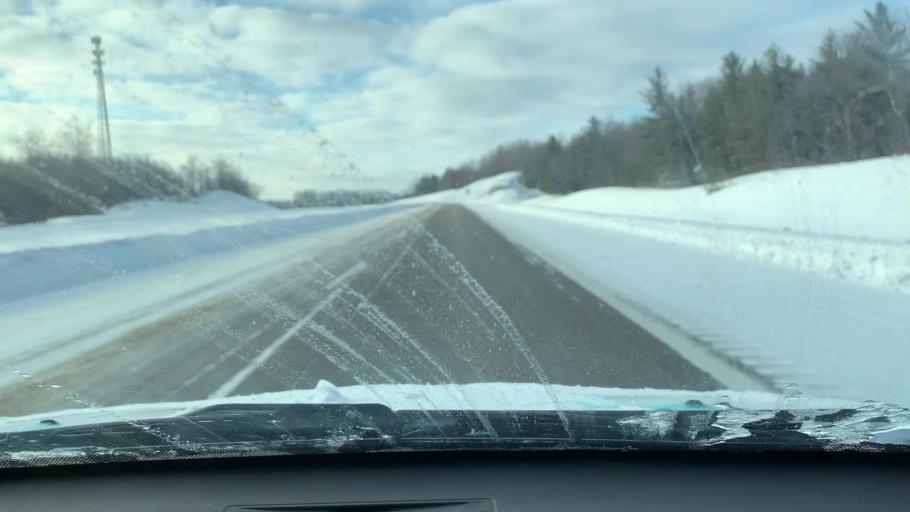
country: US
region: Michigan
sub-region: Wexford County
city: Manton
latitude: 44.3368
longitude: -85.4063
